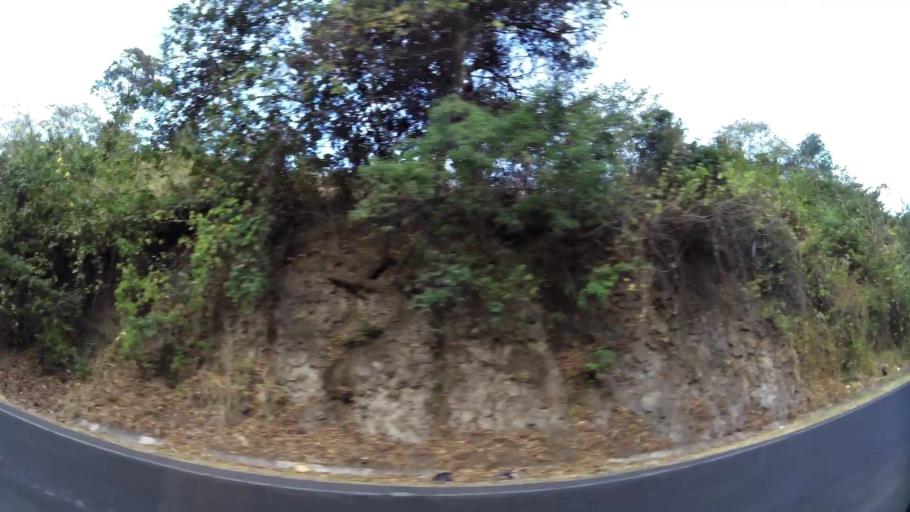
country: SV
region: San Vicente
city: Apastepeque
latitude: 13.6556
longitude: -88.7901
